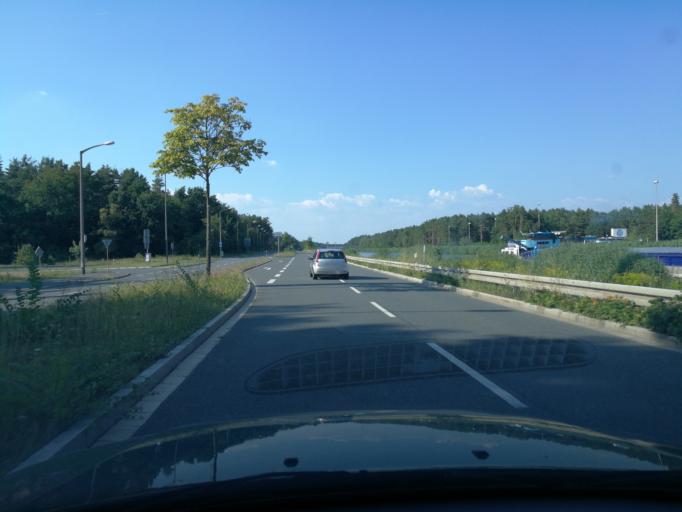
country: DE
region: Bavaria
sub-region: Regierungsbezirk Mittelfranken
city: Erlangen
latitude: 49.6015
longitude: 10.9716
